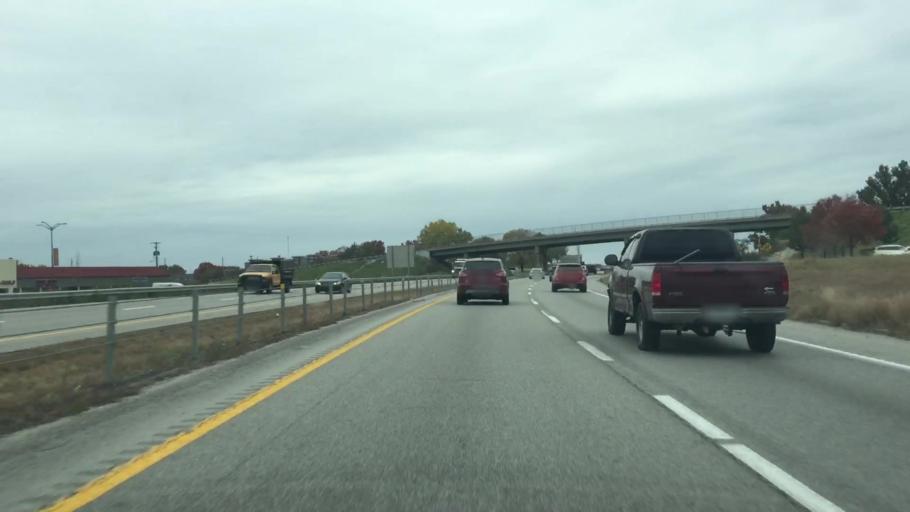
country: US
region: Missouri
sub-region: Jackson County
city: Lees Summit
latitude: 38.9174
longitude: -94.4006
